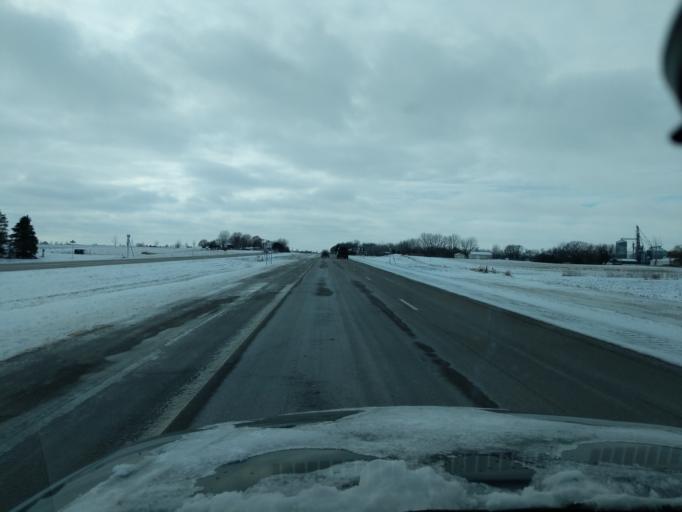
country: US
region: Minnesota
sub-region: Carver County
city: Norwood (historical)
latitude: 44.7682
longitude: -94.0290
